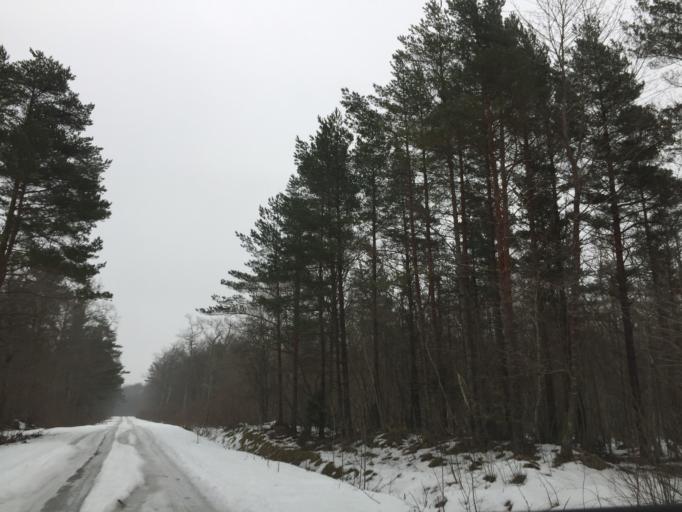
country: EE
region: Saare
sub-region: Kuressaare linn
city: Kuressaare
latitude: 58.2727
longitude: 22.5616
